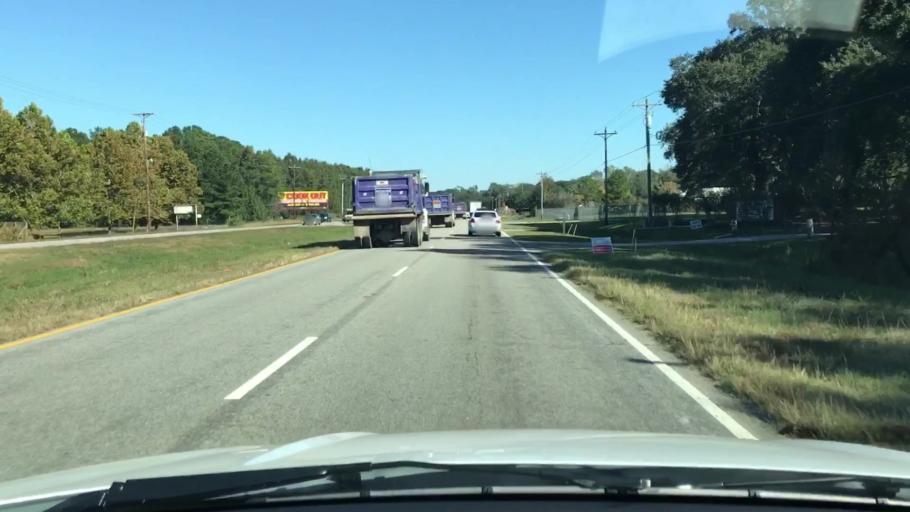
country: US
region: South Carolina
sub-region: Charleston County
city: Shell Point
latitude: 32.7809
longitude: -80.1589
